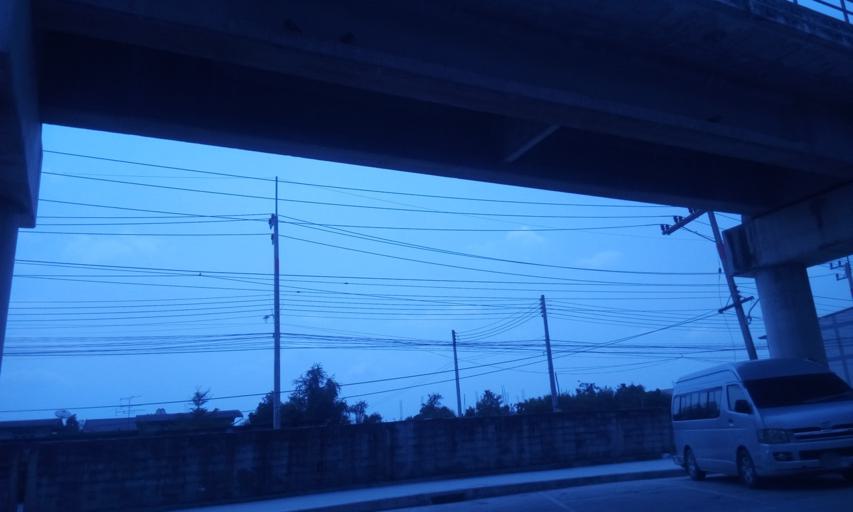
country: TH
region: Chachoengsao
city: Chachoengsao
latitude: 13.6970
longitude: 101.0894
